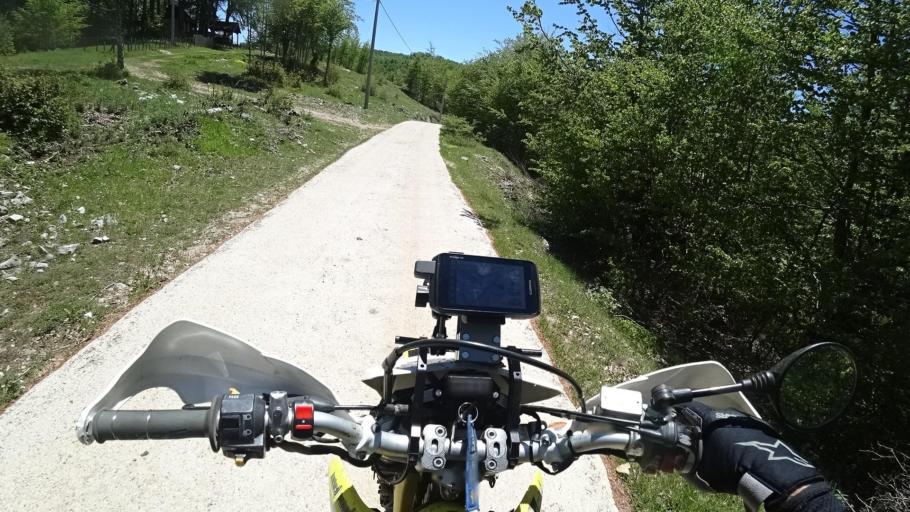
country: BA
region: Federation of Bosnia and Herzegovina
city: Polje-Bijela
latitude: 43.6492
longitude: 18.0668
